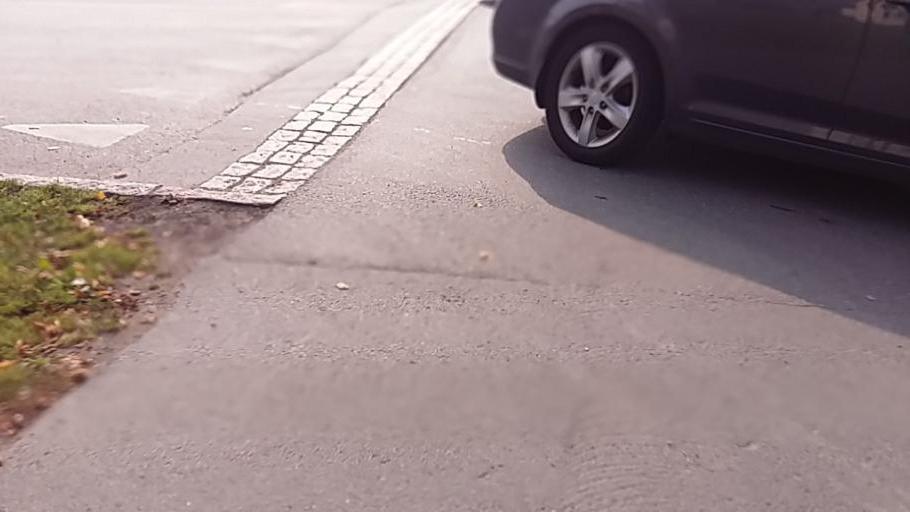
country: SE
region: Joenkoeping
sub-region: Jonkopings Kommun
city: Jonkoping
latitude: 57.7733
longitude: 14.1570
